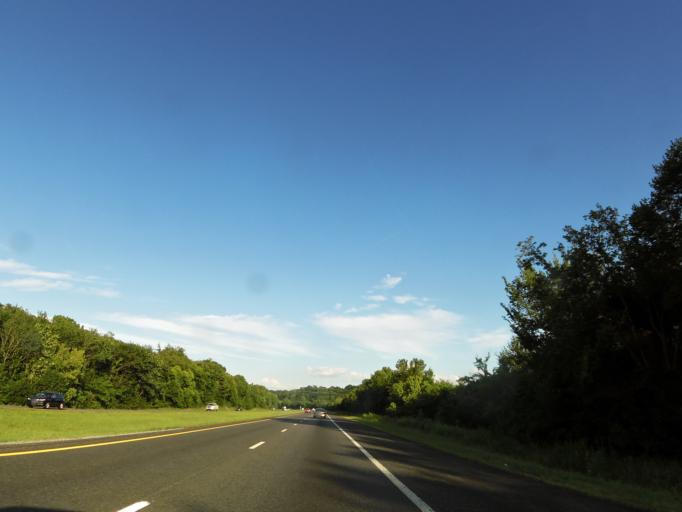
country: US
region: Tennessee
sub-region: Wilson County
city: Watertown
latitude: 36.1736
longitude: -86.1348
